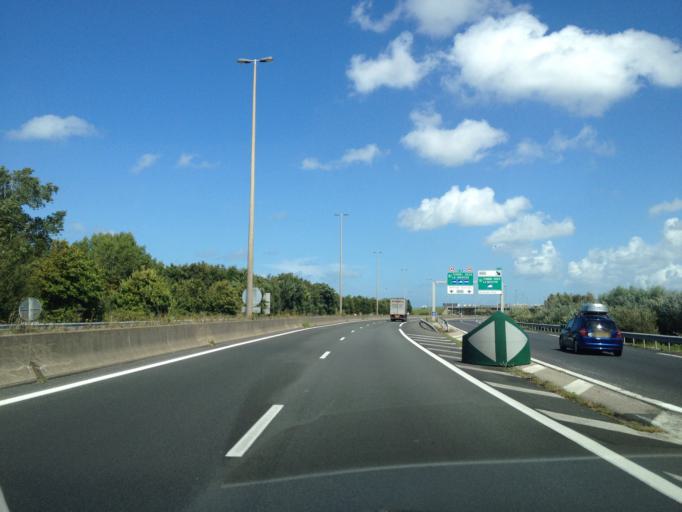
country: FR
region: Nord-Pas-de-Calais
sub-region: Departement du Pas-de-Calais
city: Coquelles
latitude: 50.9383
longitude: 1.8072
